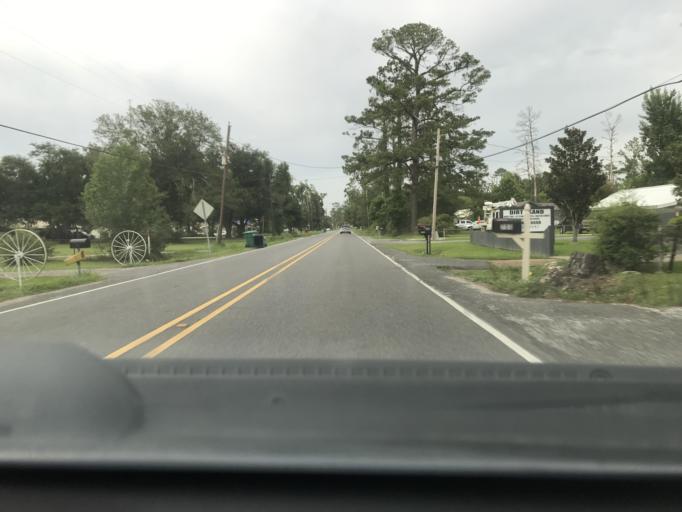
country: US
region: Louisiana
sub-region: Calcasieu Parish
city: Westlake
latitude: 30.2848
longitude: -93.2561
